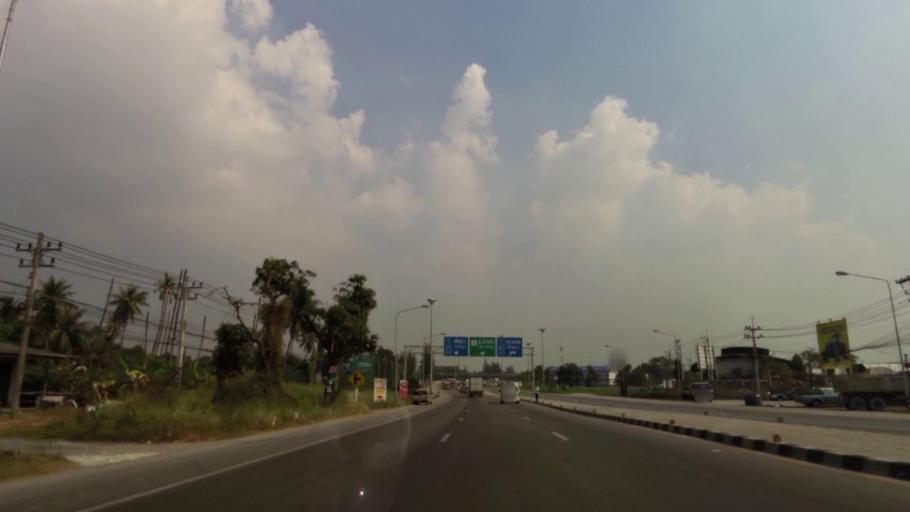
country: TH
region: Chon Buri
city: Chon Buri
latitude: 13.3471
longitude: 101.0240
